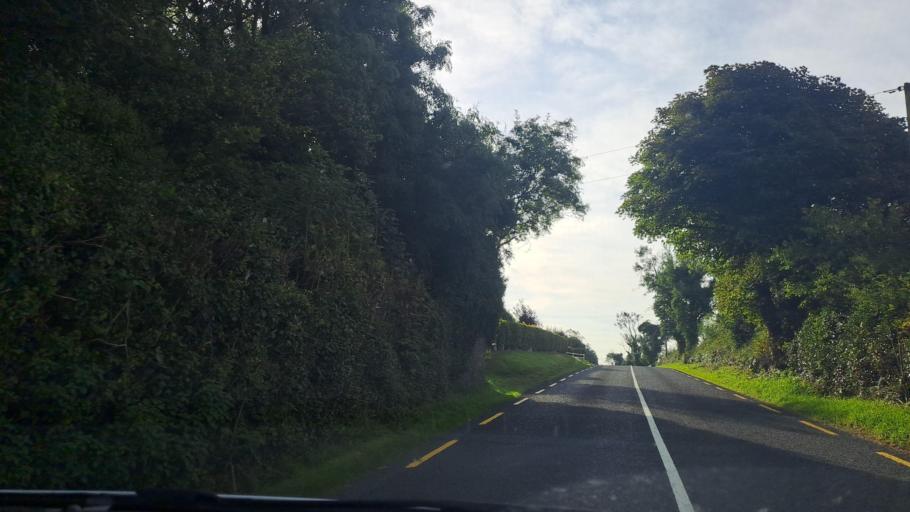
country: IE
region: Ulster
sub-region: An Cabhan
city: Kingscourt
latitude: 53.9421
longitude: -6.8329
